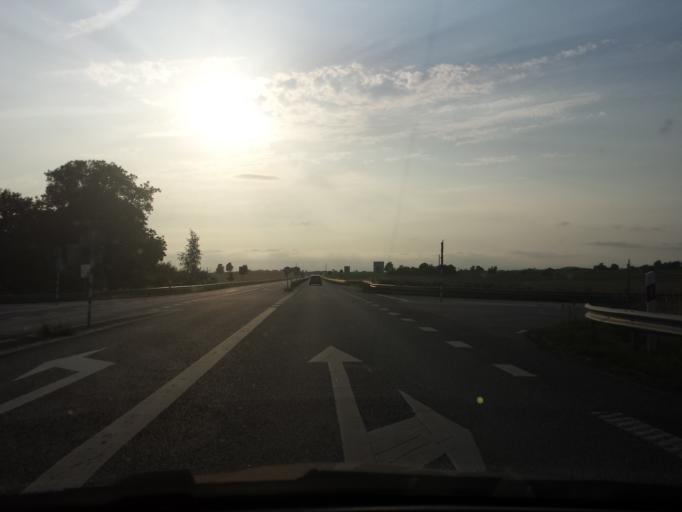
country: SE
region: Skane
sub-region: Skurups Kommun
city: Rydsgard
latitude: 55.4786
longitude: 13.6305
